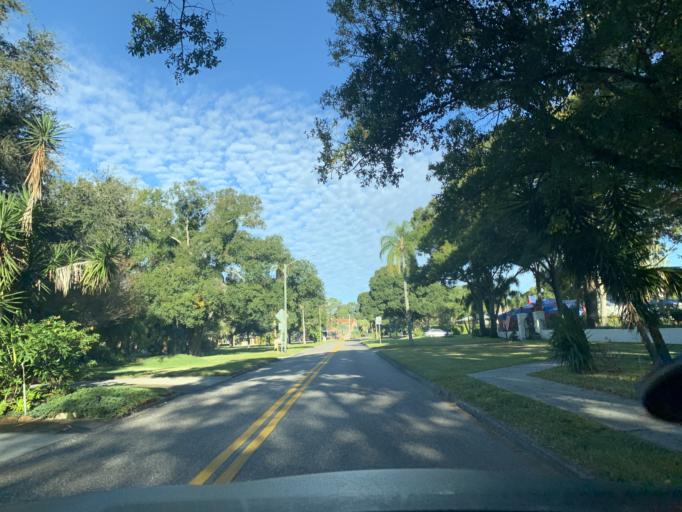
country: US
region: Florida
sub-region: Pinellas County
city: South Pasadena
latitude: 27.7652
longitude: -82.7390
